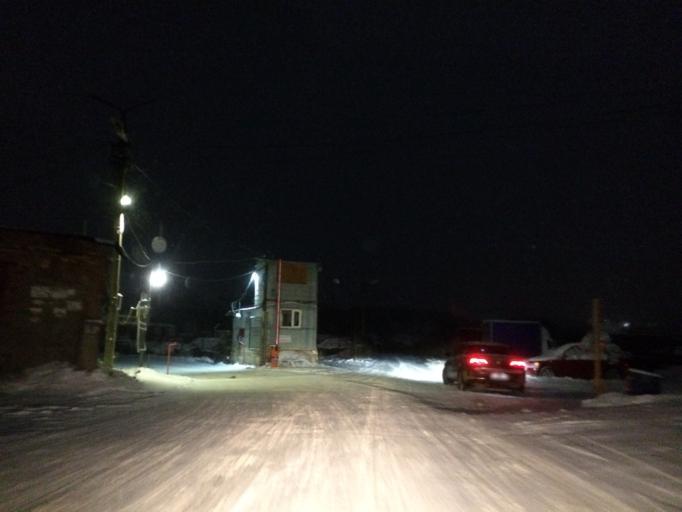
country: RU
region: Tula
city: Mendeleyevskiy
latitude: 54.1556
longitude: 37.6117
